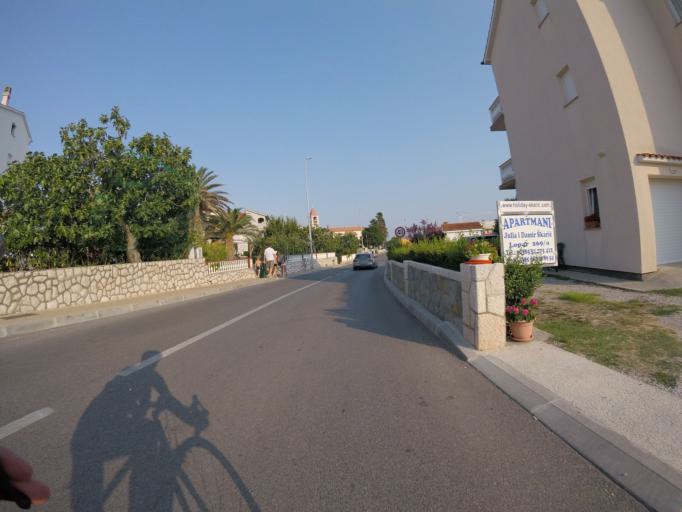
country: HR
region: Primorsko-Goranska
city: Lopar
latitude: 44.8310
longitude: 14.7302
